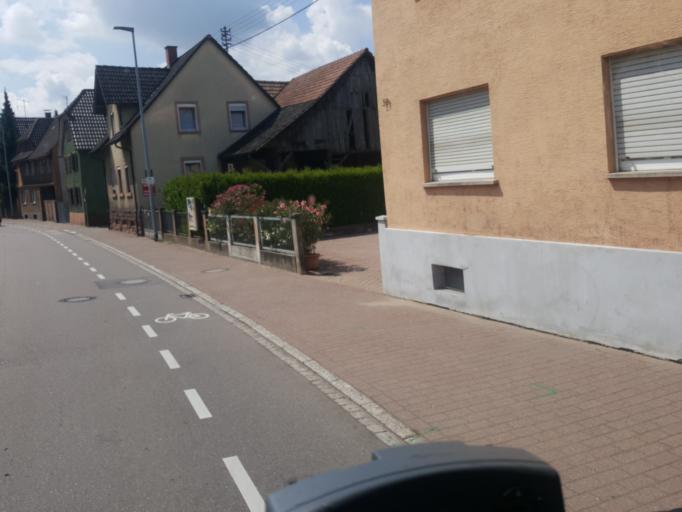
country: DE
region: Baden-Wuerttemberg
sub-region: Freiburg Region
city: Kippenheim
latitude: 48.2977
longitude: 7.8255
